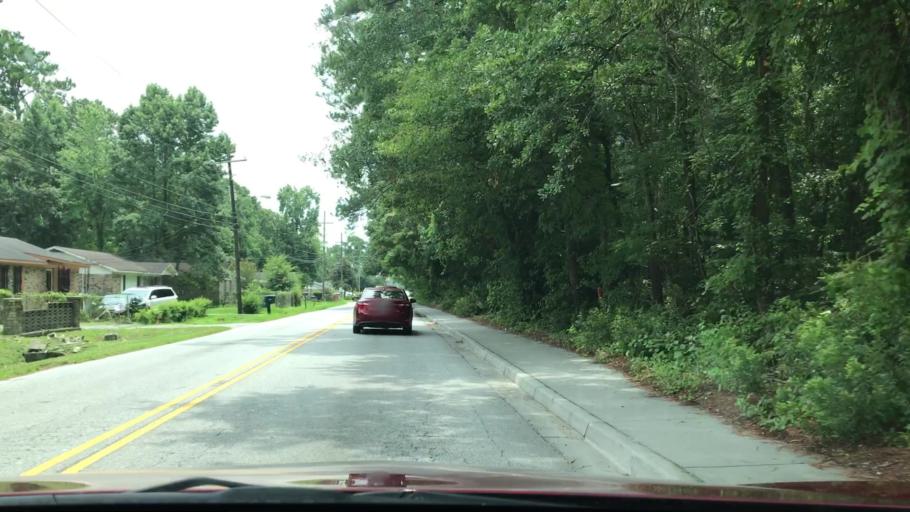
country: US
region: South Carolina
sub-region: Charleston County
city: North Charleston
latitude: 32.8039
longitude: -80.0295
